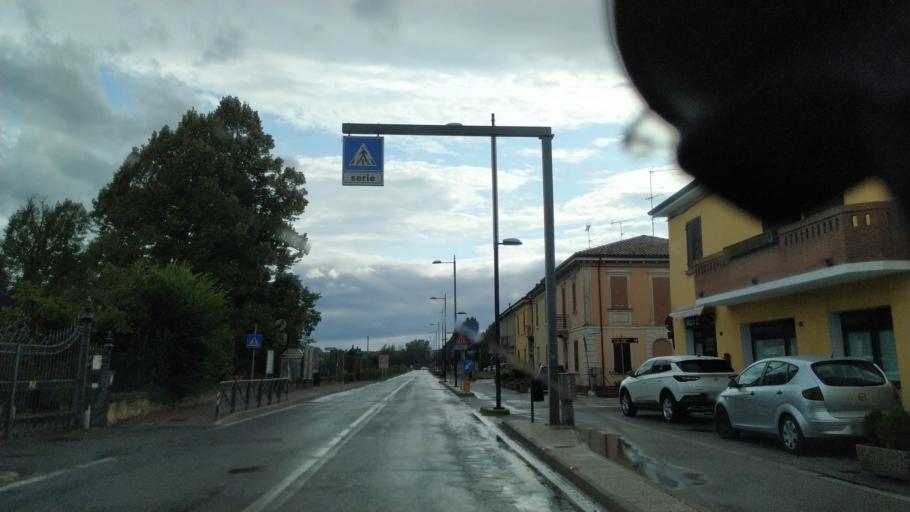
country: IT
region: Emilia-Romagna
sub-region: Provincia di Ferrara
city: Mirabello
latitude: 44.8236
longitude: 11.4579
